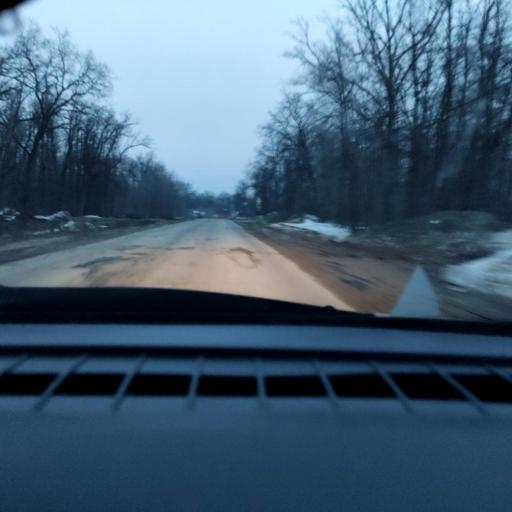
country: RU
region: Samara
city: Volzhskiy
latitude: 53.3533
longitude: 50.2044
